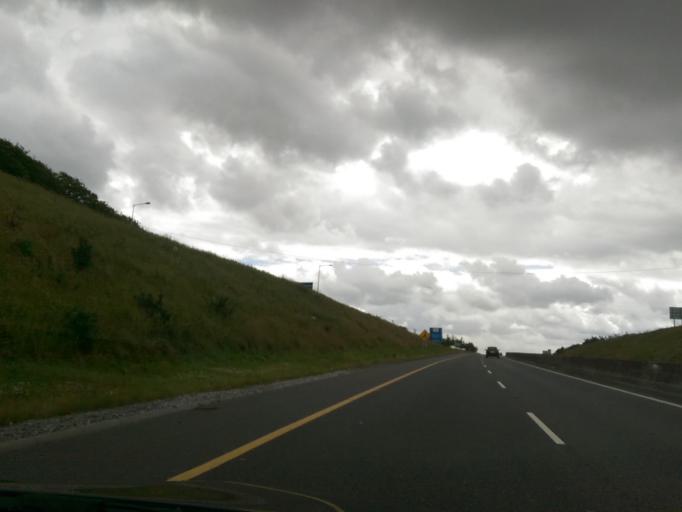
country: IE
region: Munster
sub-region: County Cork
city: Fermoy
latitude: 52.1622
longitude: -8.2659
